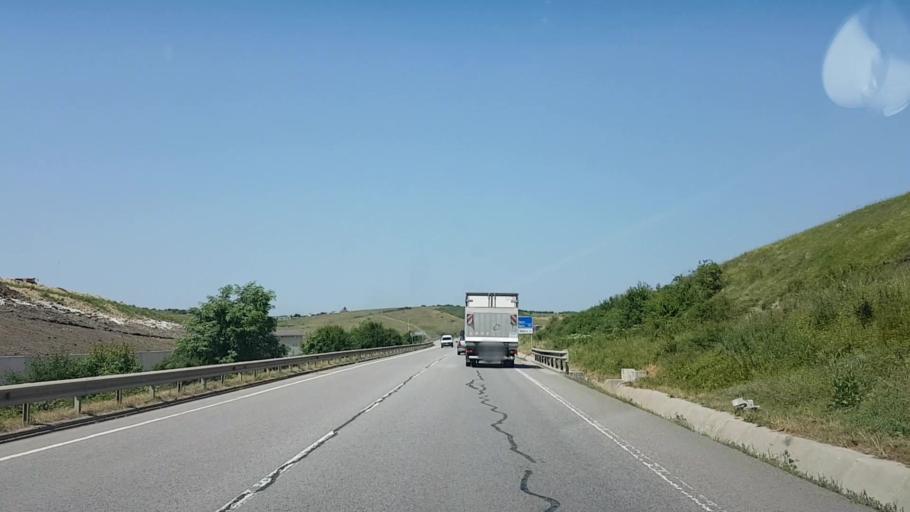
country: RO
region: Cluj
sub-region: Comuna Apahida
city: Dezmir
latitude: 46.7649
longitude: 23.6903
